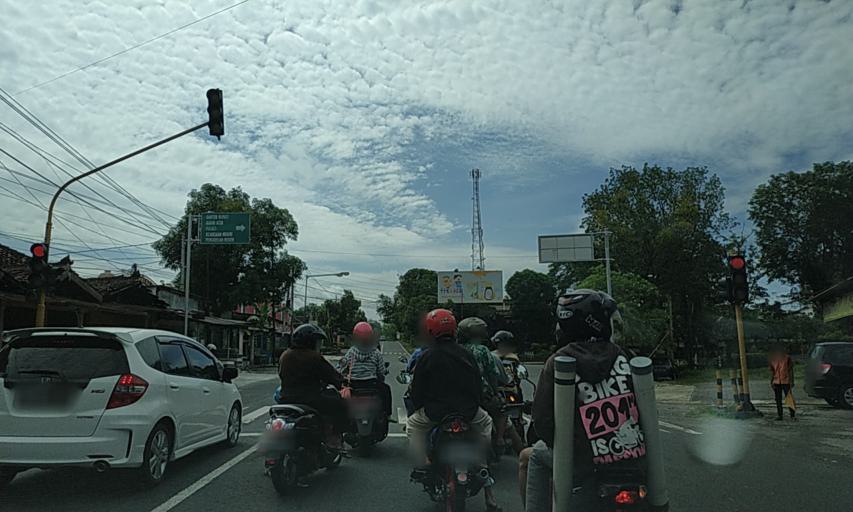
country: ID
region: Central Java
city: Selogiri
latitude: -7.7939
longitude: 110.9041
